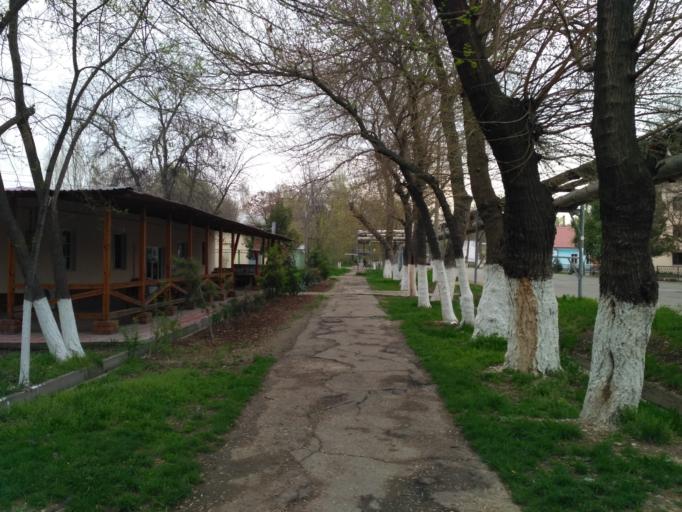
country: UZ
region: Toshkent Shahri
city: Tashkent
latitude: 41.2684
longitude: 69.2786
